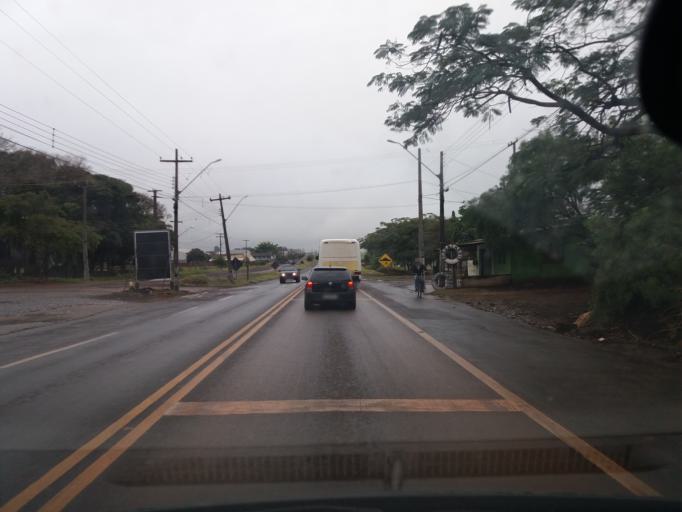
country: BR
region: Parana
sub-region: Peabiru
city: Peabiru
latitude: -23.9122
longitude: -52.3356
